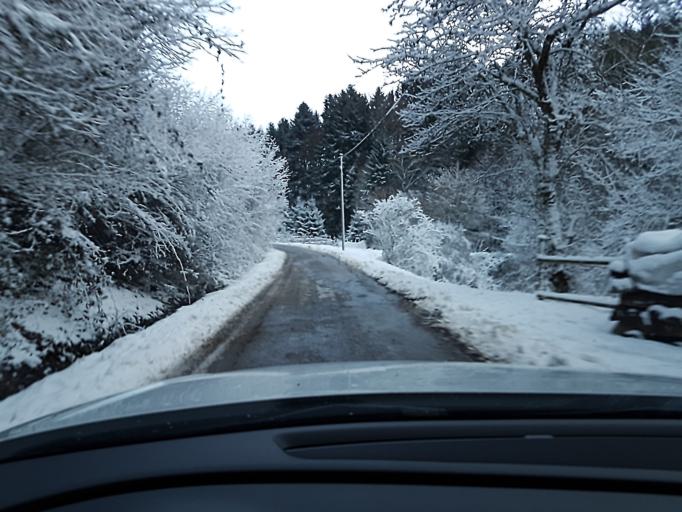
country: DE
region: Baden-Wuerttemberg
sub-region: Regierungsbezirk Stuttgart
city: Fichtenberg
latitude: 48.9517
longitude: 9.6856
